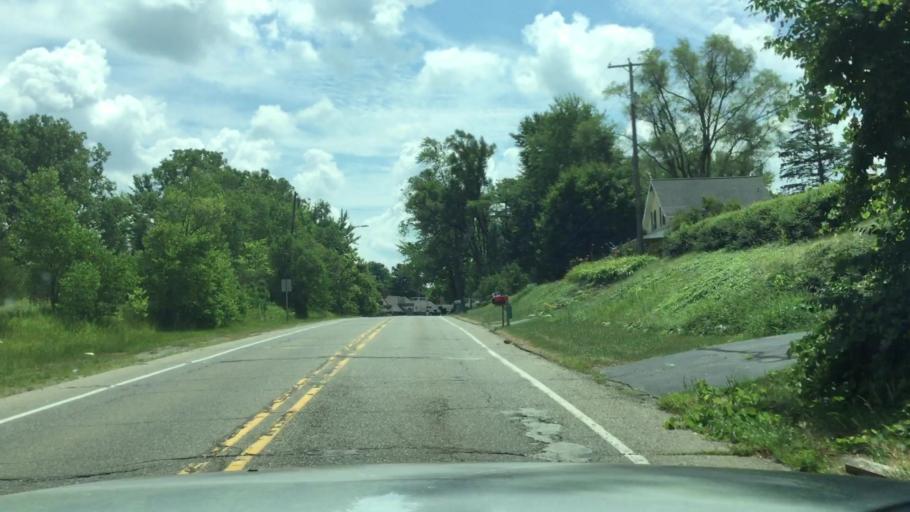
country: US
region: Michigan
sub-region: Genesee County
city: Flushing
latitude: 43.0647
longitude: -83.8643
